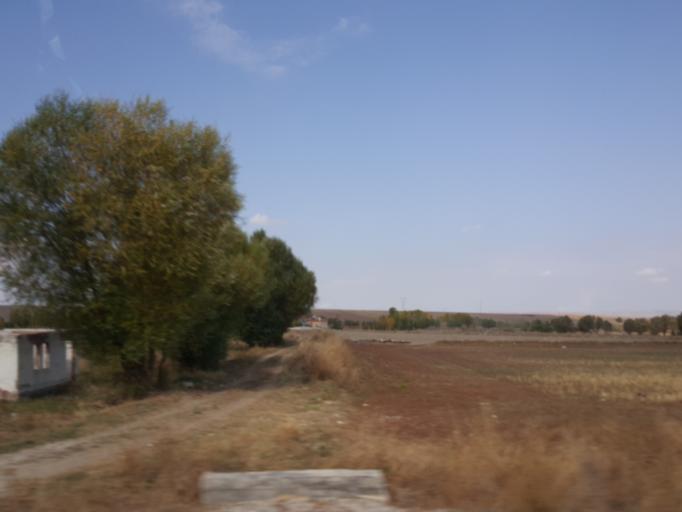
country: TR
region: Corum
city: Alaca
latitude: 40.1411
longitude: 34.8232
